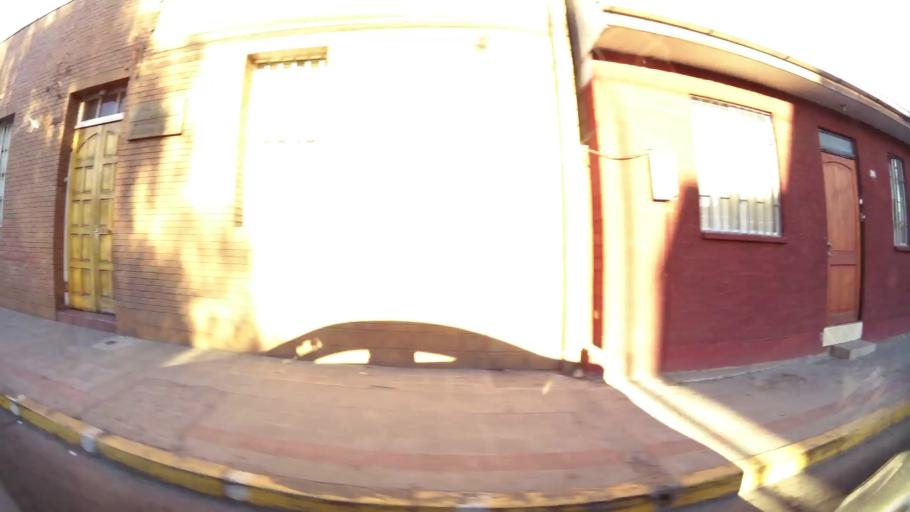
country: CL
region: Maule
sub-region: Provincia de Curico
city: Curico
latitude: -34.9880
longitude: -71.2425
